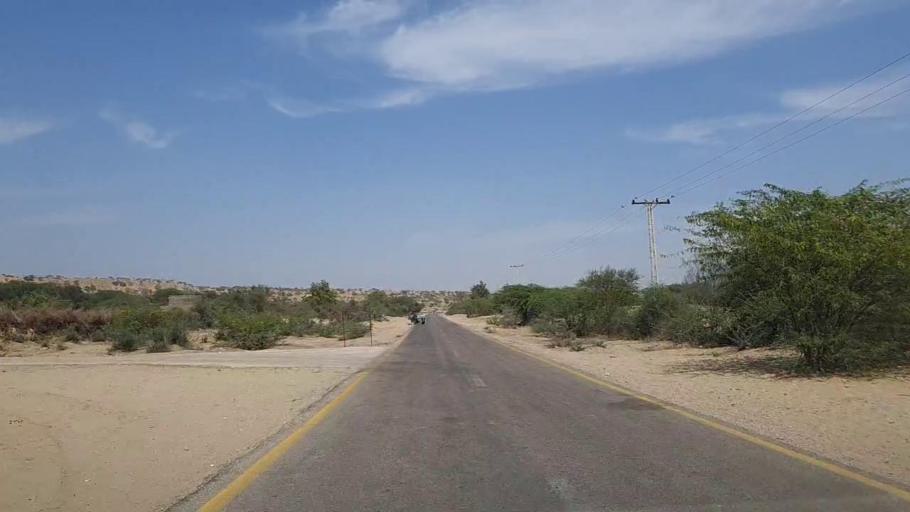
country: PK
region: Sindh
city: Mithi
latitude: 24.7969
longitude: 69.8149
